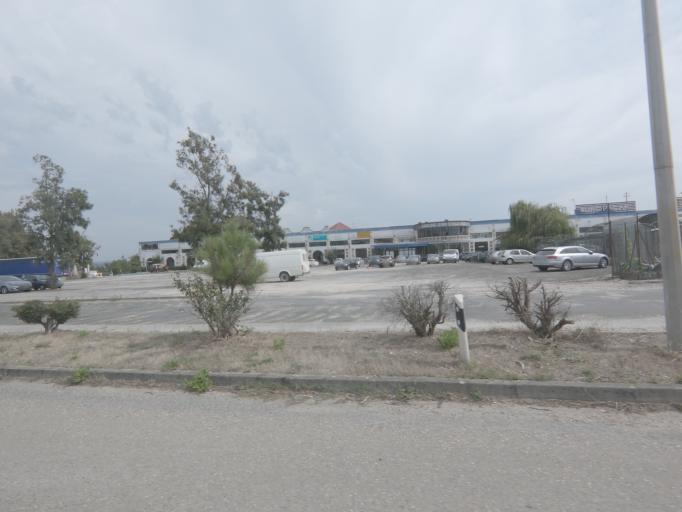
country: PT
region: Leiria
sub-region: Pombal
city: Pombal
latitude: 39.8937
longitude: -8.6576
